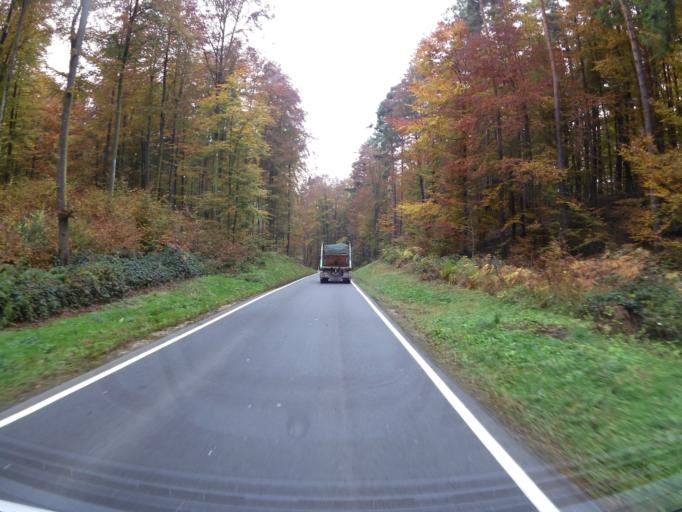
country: DE
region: Baden-Wuerttemberg
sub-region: Freiburg Region
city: Moos
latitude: 47.7016
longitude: 8.9217
